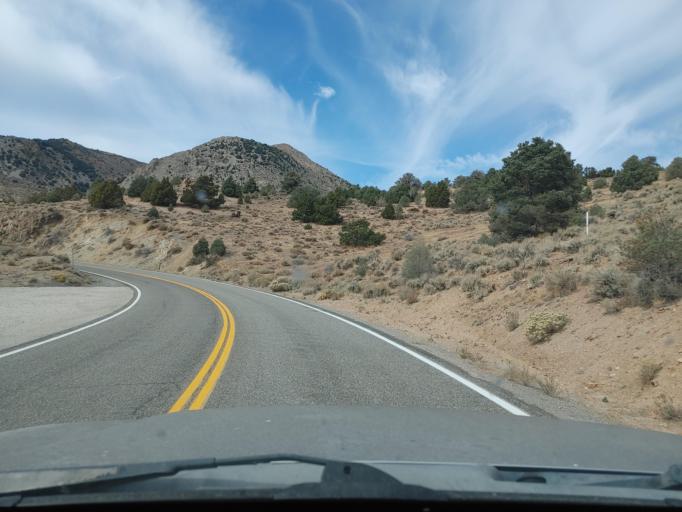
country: US
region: Nevada
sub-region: Storey County
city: Virginia City
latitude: 39.2977
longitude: -119.6447
